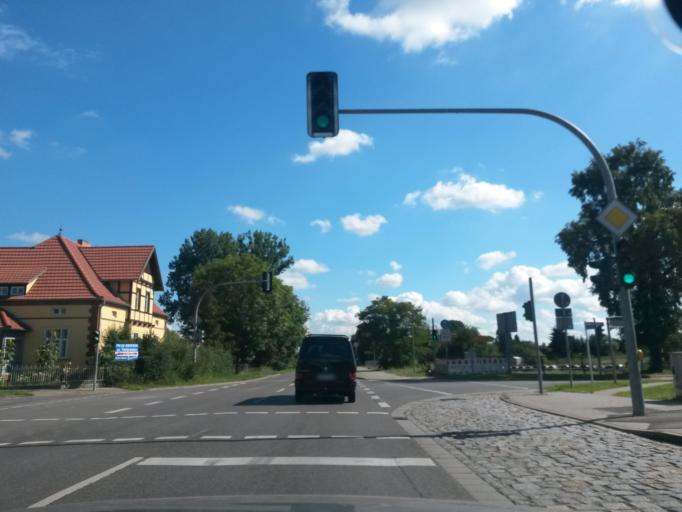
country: DE
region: Brandenburg
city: Angermunde
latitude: 53.0208
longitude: 14.0334
